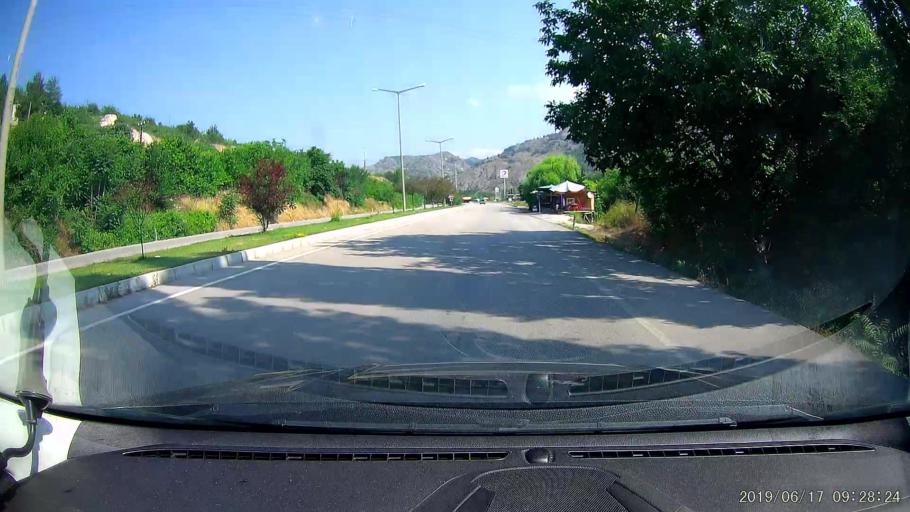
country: TR
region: Amasya
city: Amasya
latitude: 40.6879
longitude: 35.8224
